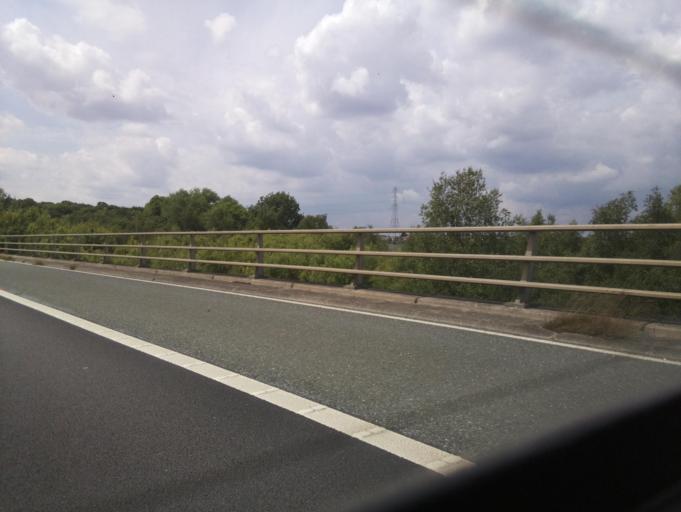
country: GB
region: England
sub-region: City and Borough of Wakefield
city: Ferrybridge
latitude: 53.7353
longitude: -1.2872
